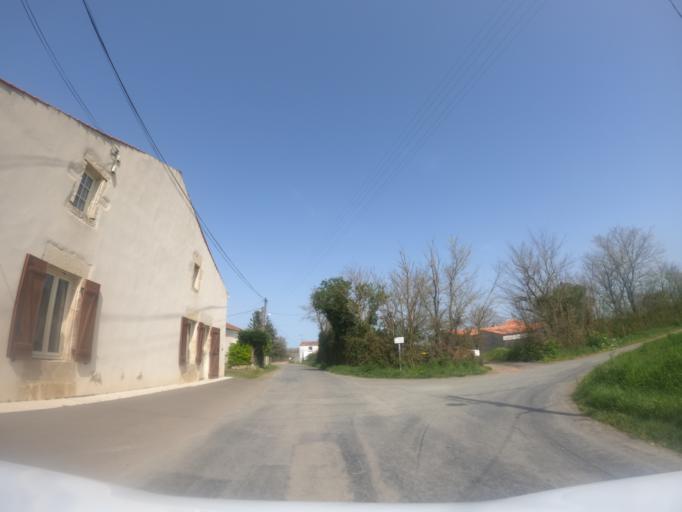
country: FR
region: Pays de la Loire
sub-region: Departement de la Vendee
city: Maillezais
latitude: 46.3932
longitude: -0.7968
